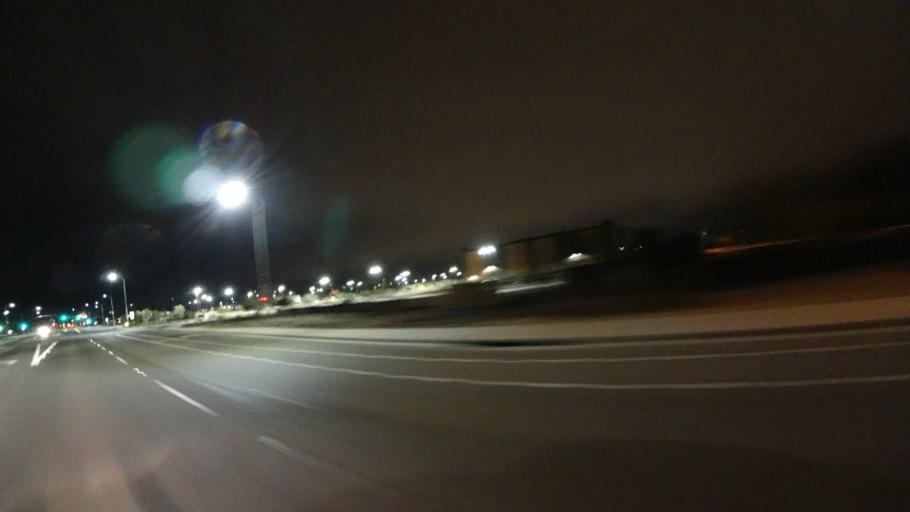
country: US
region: Arizona
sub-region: Maricopa County
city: Sun Lakes
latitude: 33.2332
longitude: -111.8386
